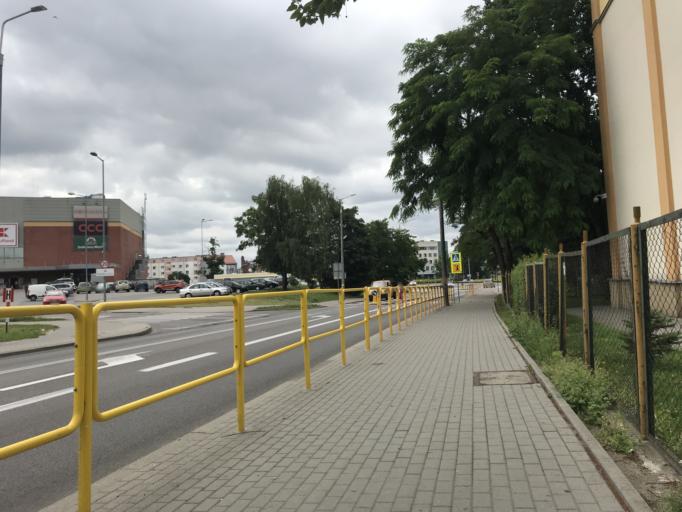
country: PL
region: Warmian-Masurian Voivodeship
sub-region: Powiat elblaski
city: Elblag
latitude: 54.1672
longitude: 19.4000
